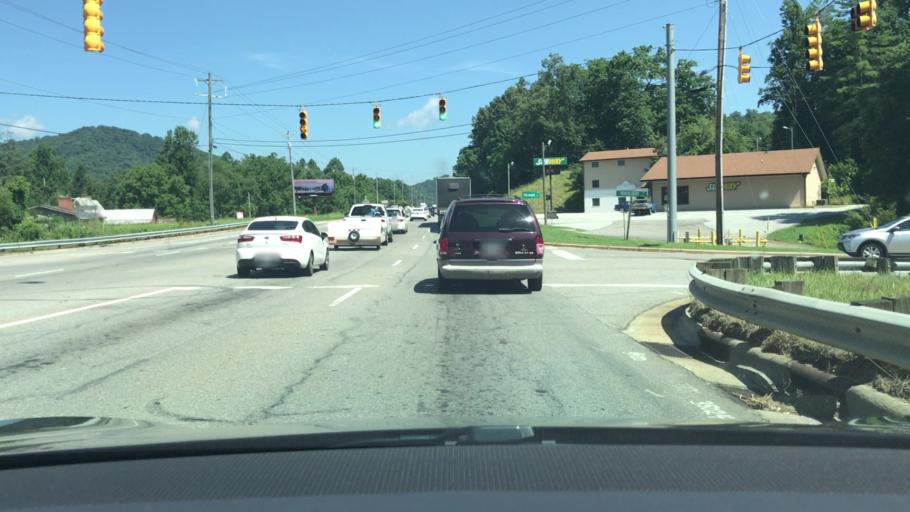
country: US
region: North Carolina
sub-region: Macon County
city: Franklin
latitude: 35.1209
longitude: -83.3925
